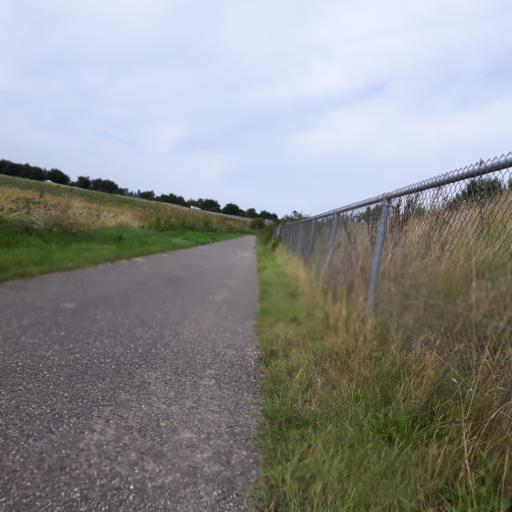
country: NL
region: Zeeland
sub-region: Gemeente Goes
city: Goes
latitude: 51.4782
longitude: 3.8974
